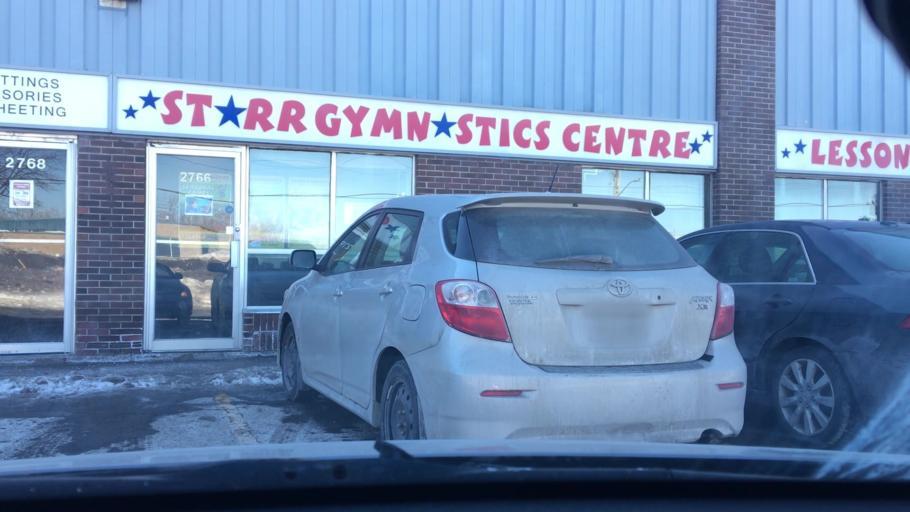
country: CA
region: Ontario
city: Ottawa
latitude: 45.3959
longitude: -75.6061
